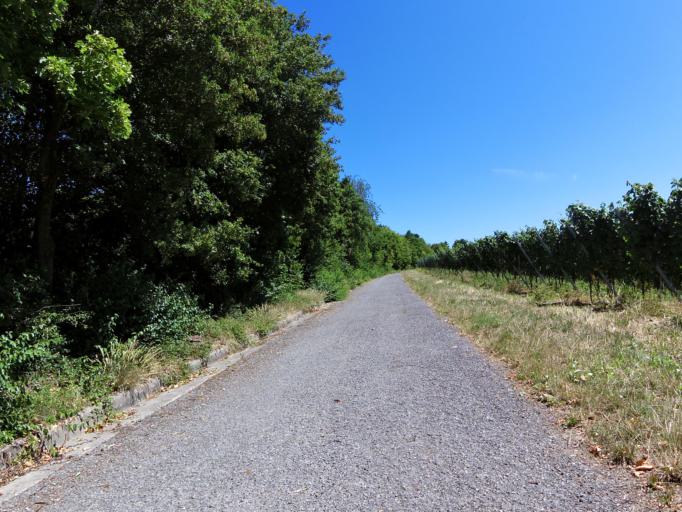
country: DE
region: Bavaria
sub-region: Regierungsbezirk Unterfranken
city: Randersacker
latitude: 49.7586
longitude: 9.9907
